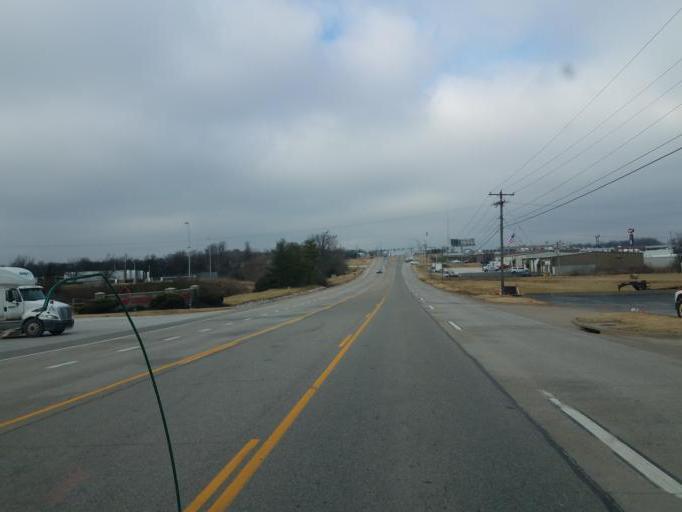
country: US
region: Missouri
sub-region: Greene County
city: Springfield
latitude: 37.2387
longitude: -93.2195
